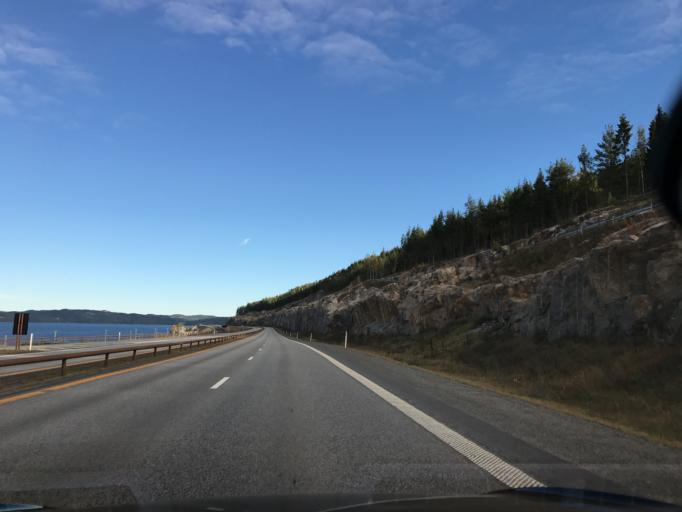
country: NO
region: Hedmark
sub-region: Stange
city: Stange
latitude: 60.5392
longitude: 11.2456
